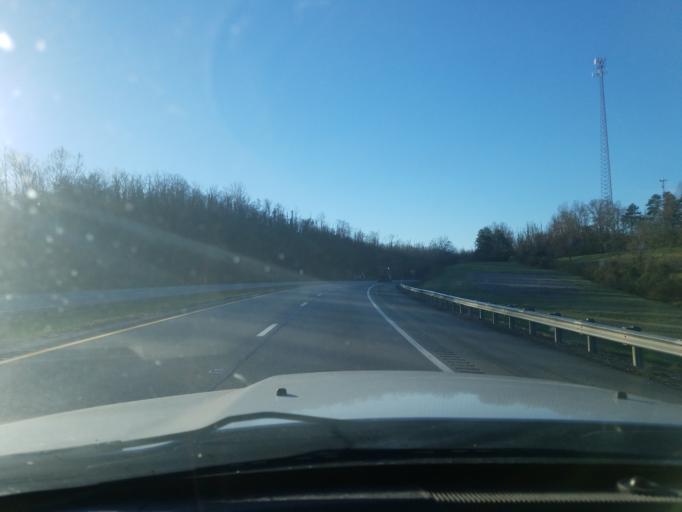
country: US
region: West Virginia
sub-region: Wood County
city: Parkersburg
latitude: 39.2769
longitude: -81.4941
